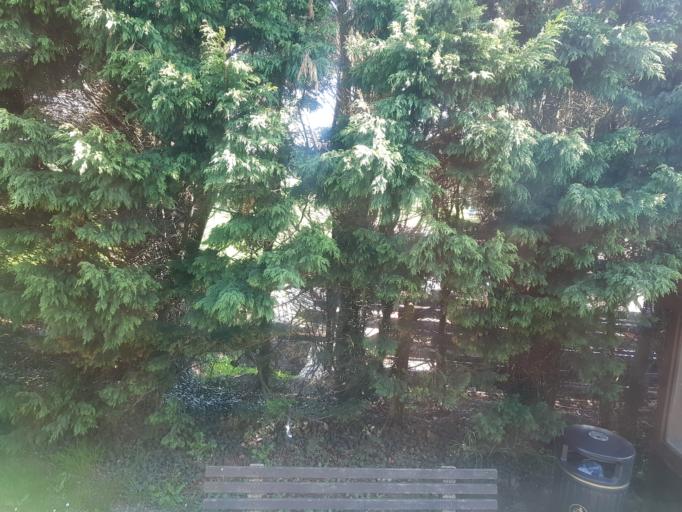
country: GB
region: England
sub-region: Isle of Wight
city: East Cowes
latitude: 50.7379
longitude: -1.2686
